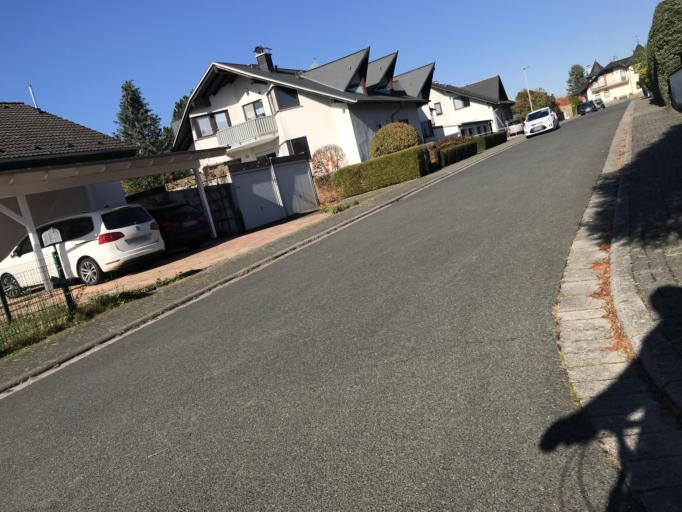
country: DE
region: Hesse
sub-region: Regierungsbezirk Giessen
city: Braunfels
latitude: 50.5209
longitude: 8.3877
